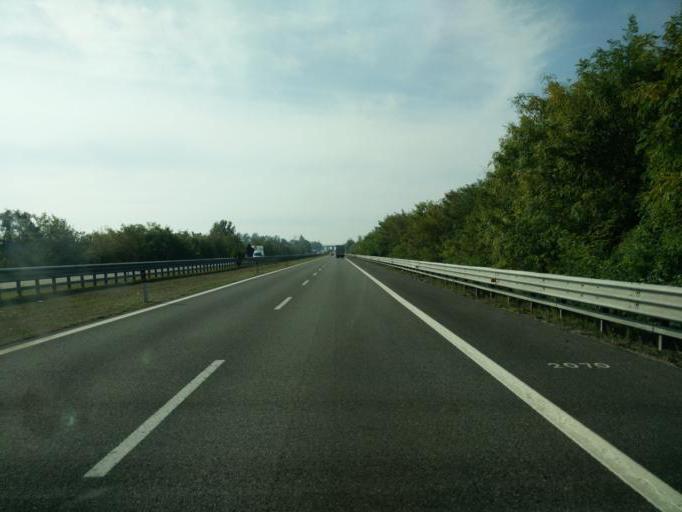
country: IT
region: Lombardy
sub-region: Provincia di Cremona
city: Corte de' Frati
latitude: 45.2457
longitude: 10.1206
